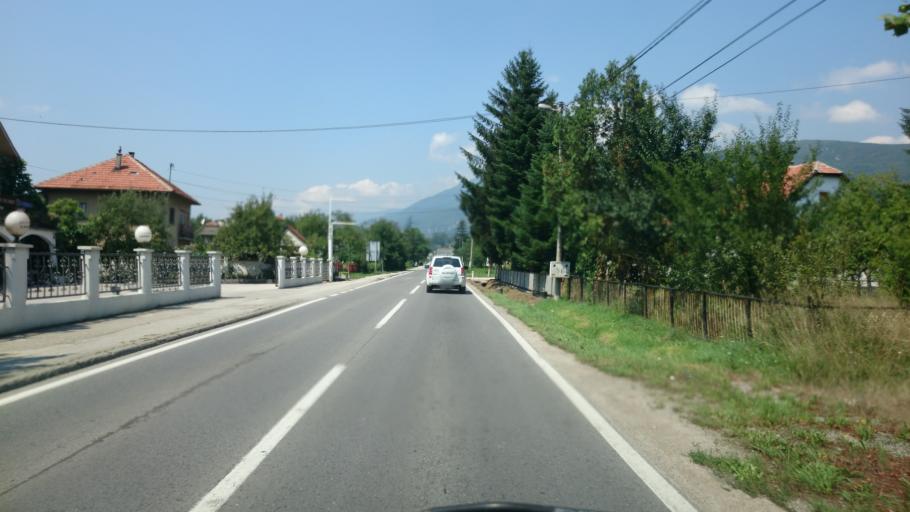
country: BA
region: Federation of Bosnia and Herzegovina
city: Travnik
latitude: 44.2081
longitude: 17.7142
